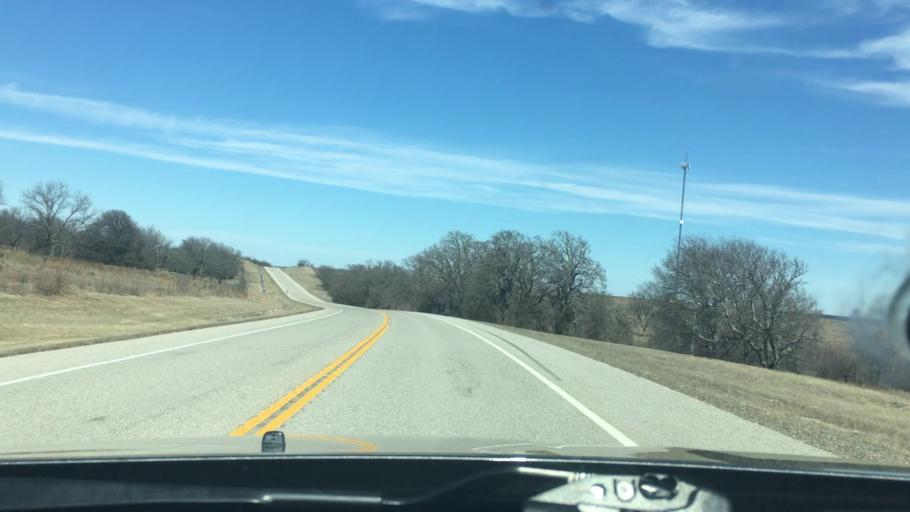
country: US
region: Oklahoma
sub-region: Carter County
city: Dickson
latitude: 34.3348
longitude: -96.9510
